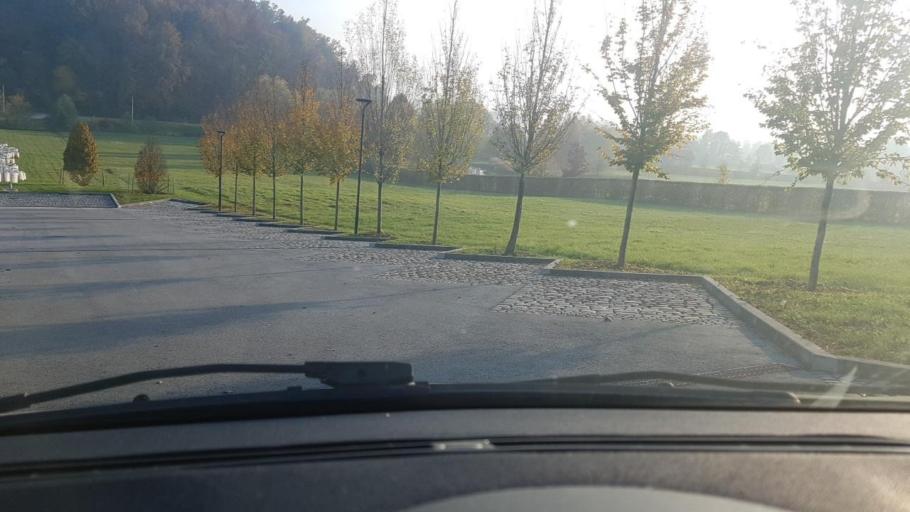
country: SI
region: Podcetrtek
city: Podcetrtek
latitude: 46.1293
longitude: 15.6165
